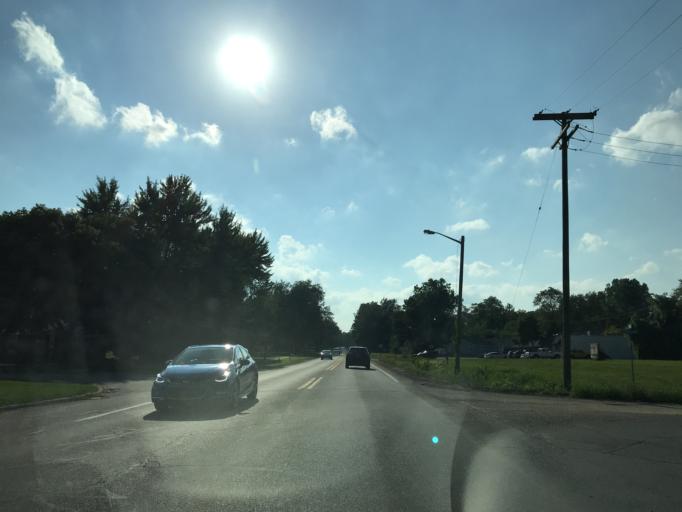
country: US
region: Michigan
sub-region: Wayne County
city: Plymouth
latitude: 42.3957
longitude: -83.4433
